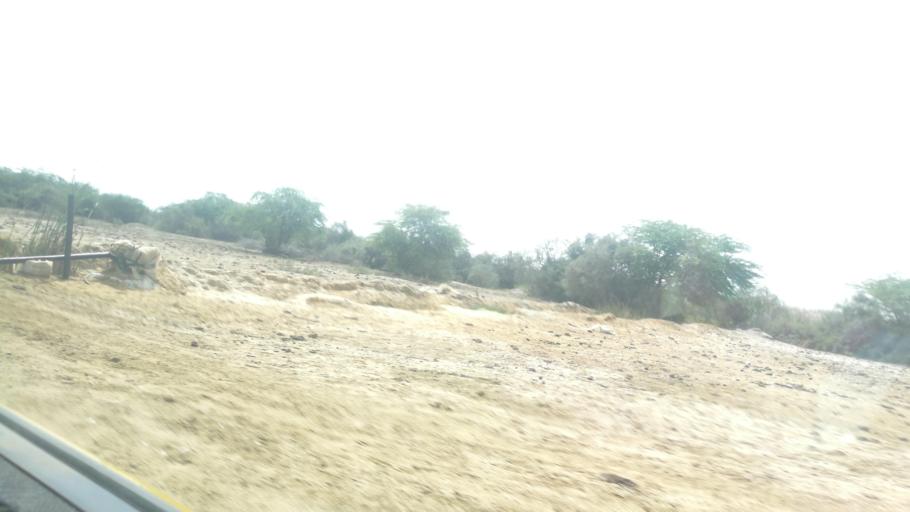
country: SN
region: Saint-Louis
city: Saint-Louis
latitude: 16.0552
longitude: -16.3296
